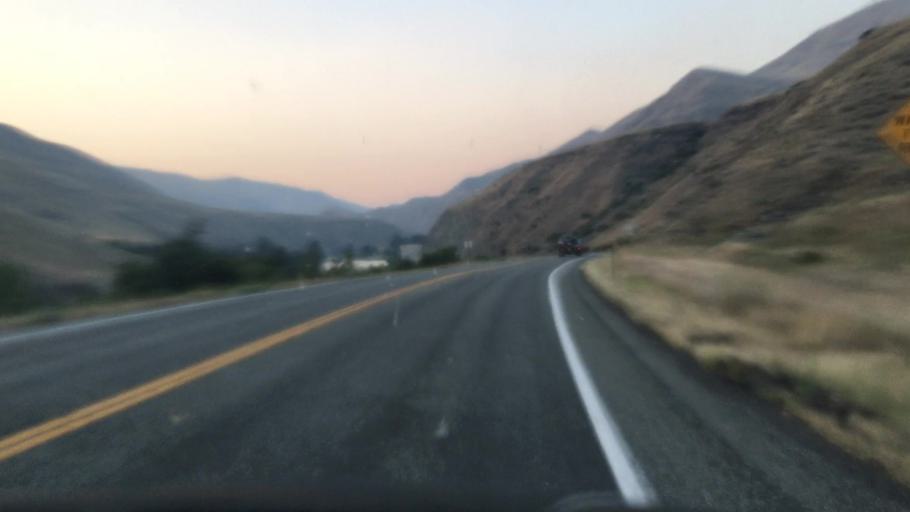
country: US
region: Idaho
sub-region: Idaho County
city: Grangeville
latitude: 45.5378
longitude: -116.3078
